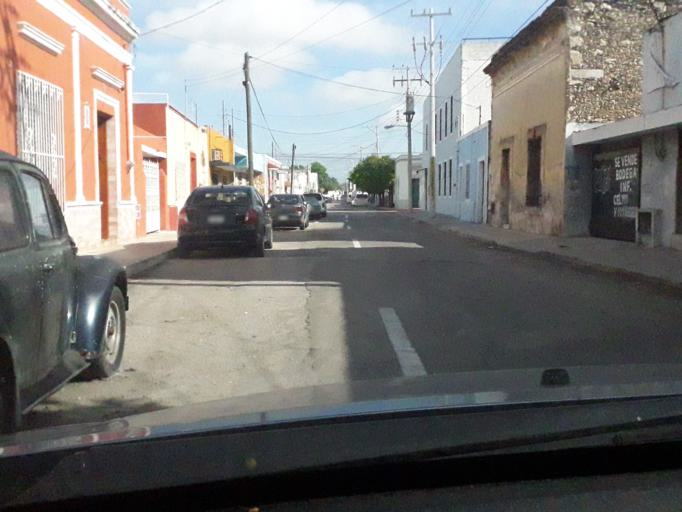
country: MX
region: Yucatan
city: Merida
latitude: 20.9567
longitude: -89.6176
